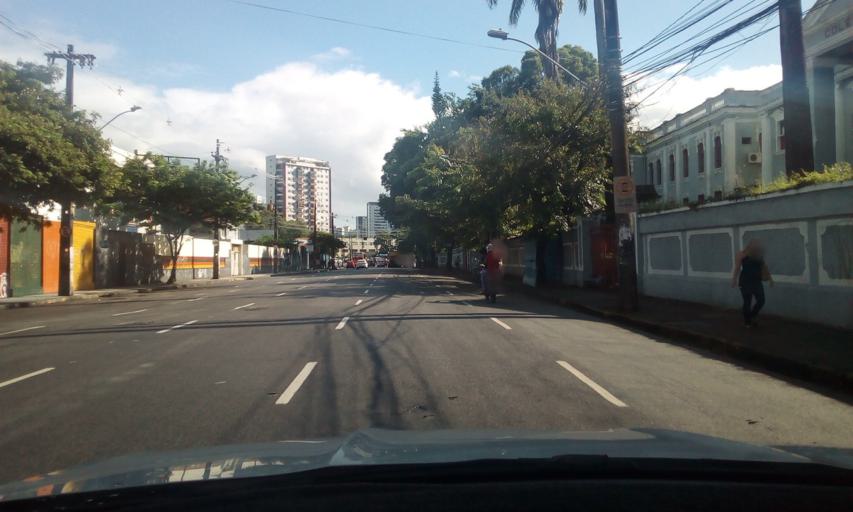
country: BR
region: Pernambuco
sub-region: Recife
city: Recife
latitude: -8.0553
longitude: -34.8956
